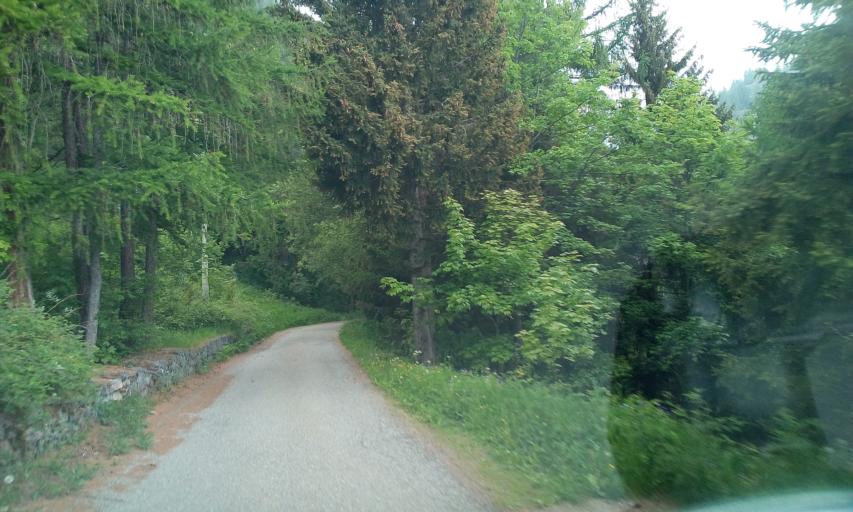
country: IT
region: Aosta Valley
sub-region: Valle d'Aosta
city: Torgnon
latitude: 45.8224
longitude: 7.5749
